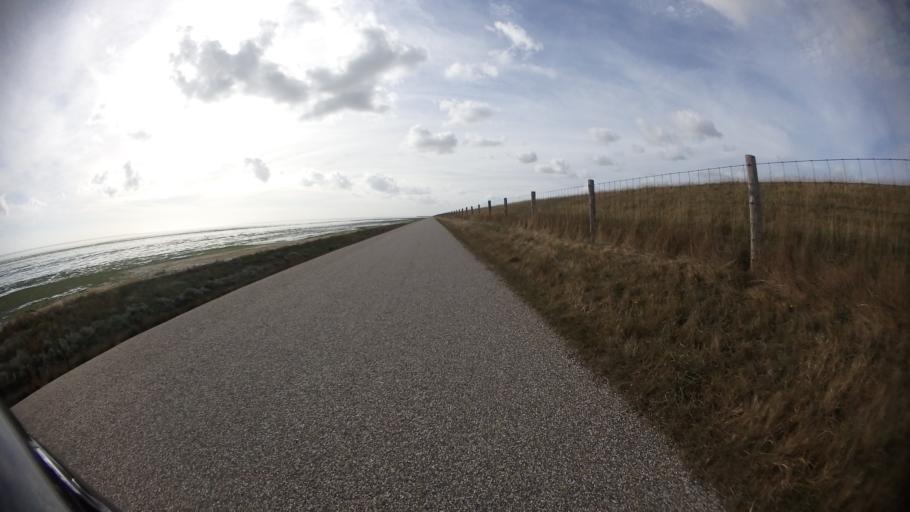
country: NL
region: North Holland
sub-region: Gemeente Texel
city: Den Burg
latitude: 53.1236
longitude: 4.8994
